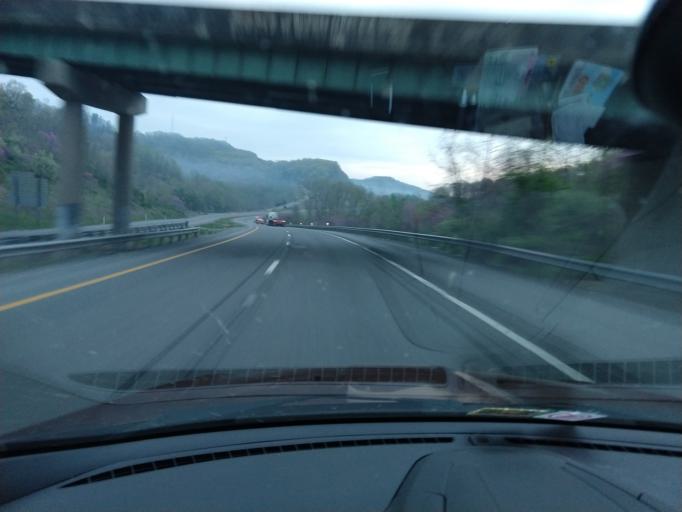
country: US
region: West Virginia
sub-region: Braxton County
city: Sutton
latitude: 38.6737
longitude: -80.7185
